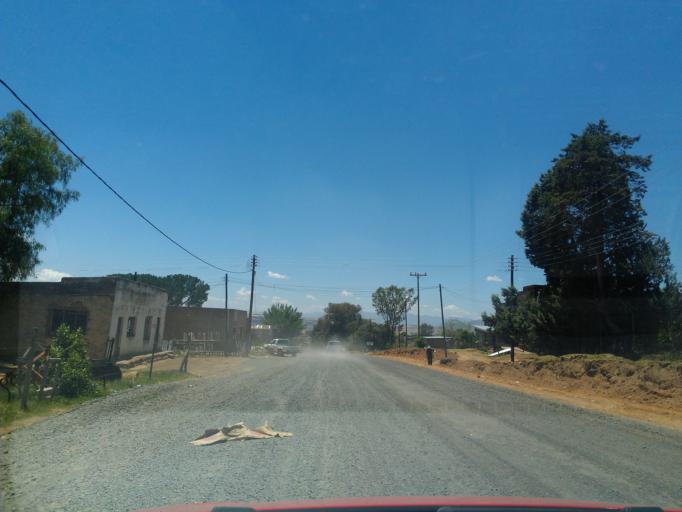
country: LS
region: Berea
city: Teyateyaneng
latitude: -29.1478
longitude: 27.7538
